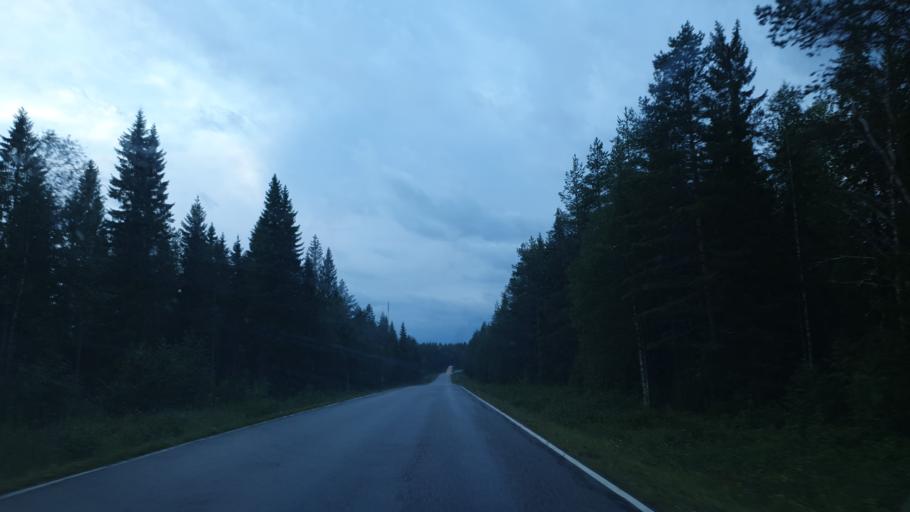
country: FI
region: Kainuu
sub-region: Kehys-Kainuu
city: Kuhmo
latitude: 63.9569
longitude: 29.7086
